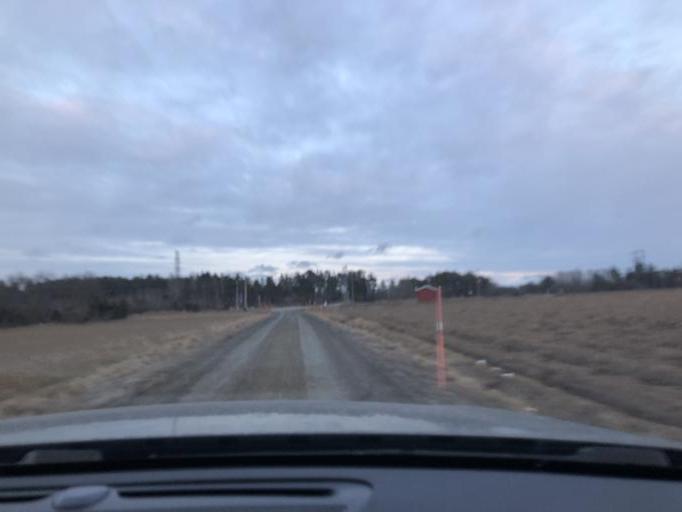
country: SE
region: Uppsala
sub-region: Uppsala Kommun
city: Gamla Uppsala
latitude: 59.9198
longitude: 17.6399
